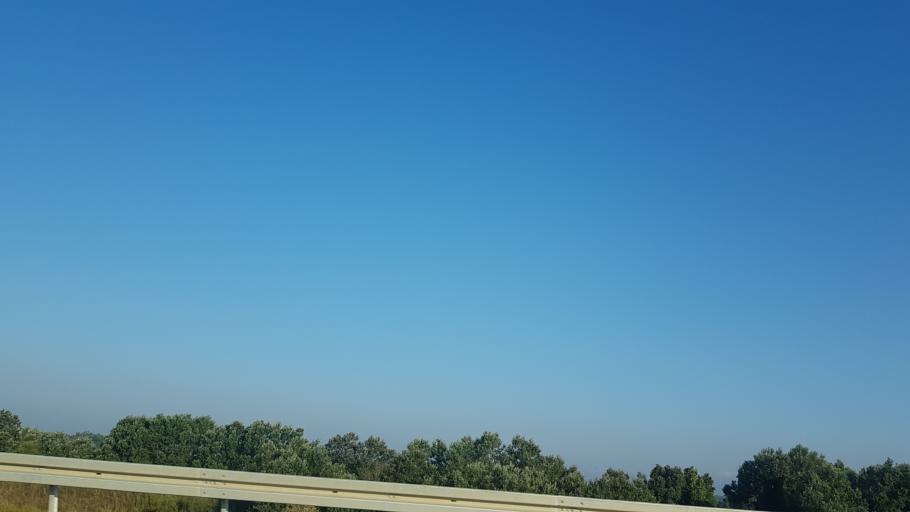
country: TR
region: Bursa
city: Karacabey
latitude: 40.1808
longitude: 28.3297
